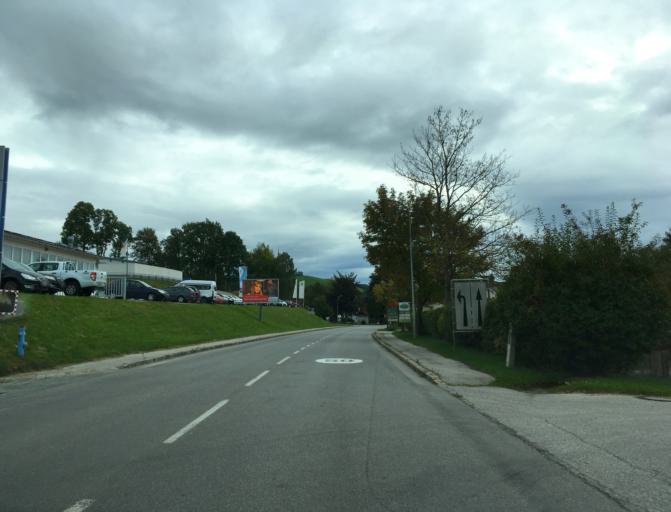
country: AT
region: Lower Austria
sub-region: Politischer Bezirk Wiener Neustadt
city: Bad Schonau
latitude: 47.5266
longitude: 16.1865
